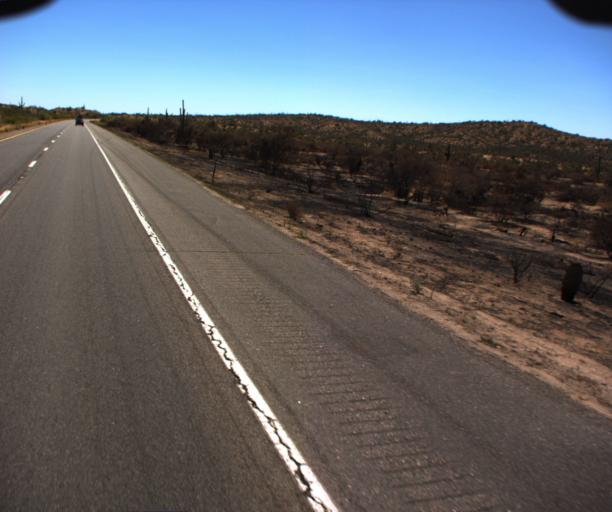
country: US
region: Arizona
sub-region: Maricopa County
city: Rio Verde
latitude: 33.6776
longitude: -111.5041
